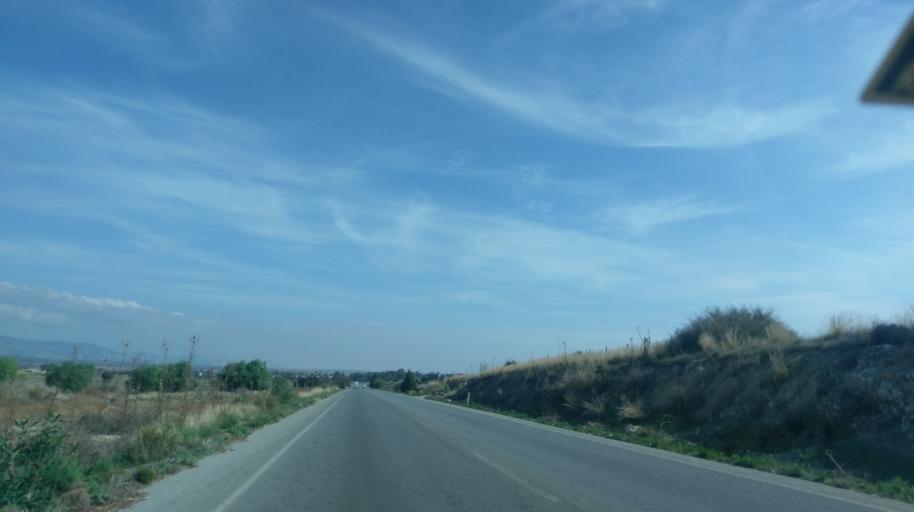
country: CY
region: Ammochostos
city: Lefkonoiko
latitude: 35.2575
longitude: 33.6426
